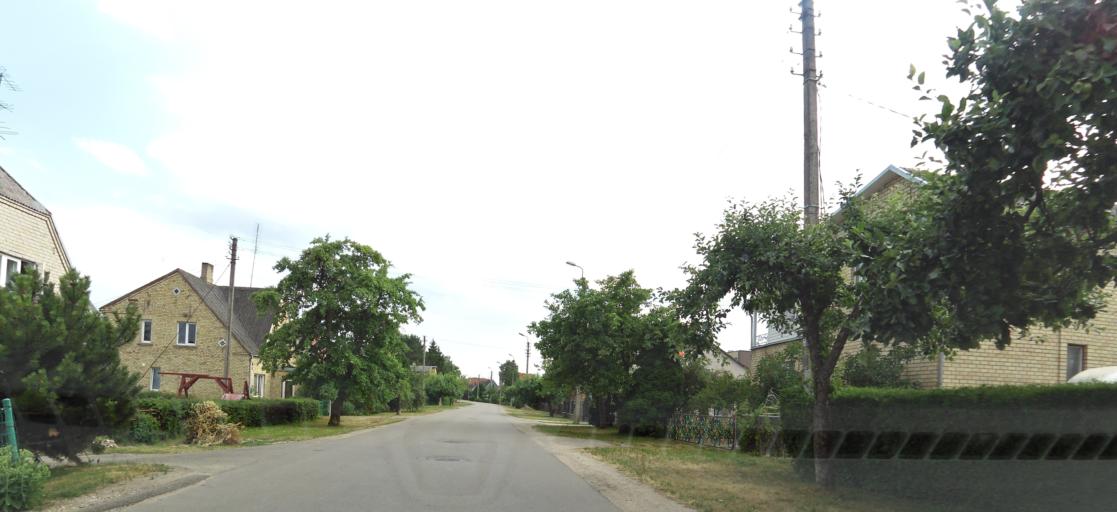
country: LT
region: Panevezys
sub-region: Birzai
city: Birzai
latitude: 56.2001
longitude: 24.7609
